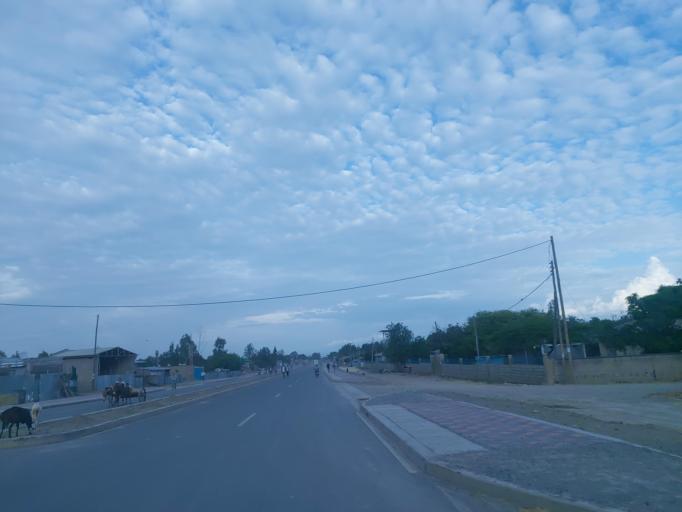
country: ET
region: Oromiya
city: Ziway
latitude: 8.1460
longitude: 38.8057
